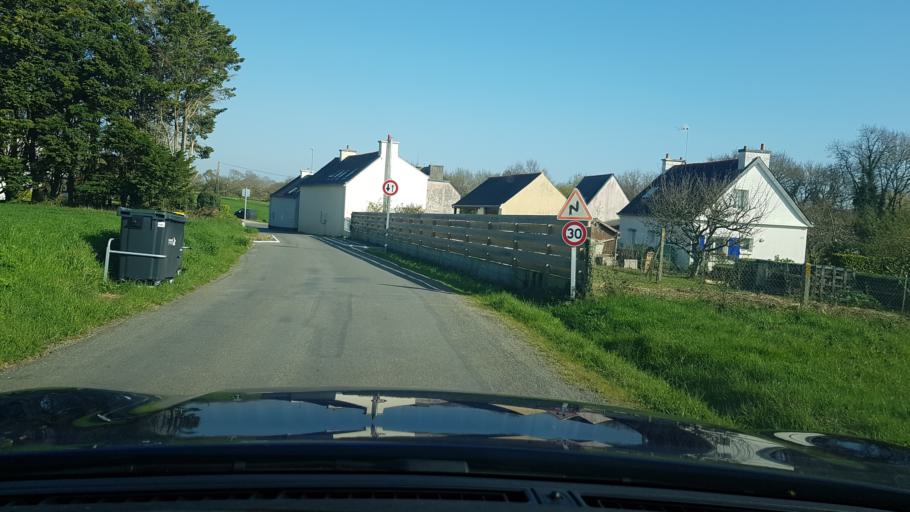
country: FR
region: Brittany
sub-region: Departement du Finistere
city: Moelan-sur-Mer
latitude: 47.7796
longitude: -3.6187
